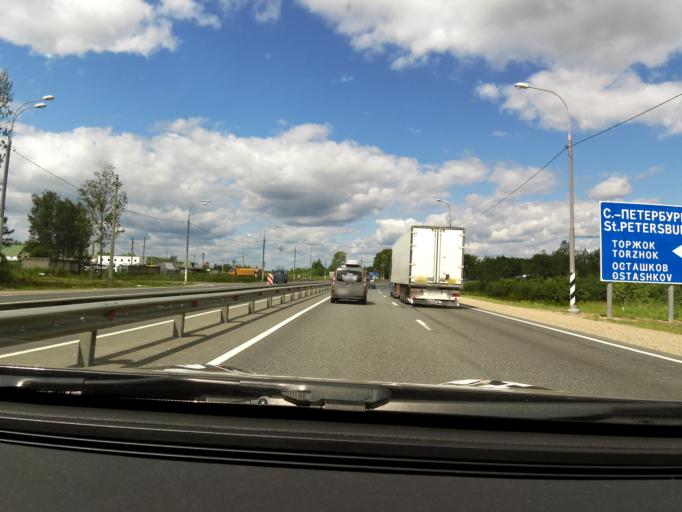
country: RU
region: Tverskaya
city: Torzhok
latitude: 57.0222
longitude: 35.0401
